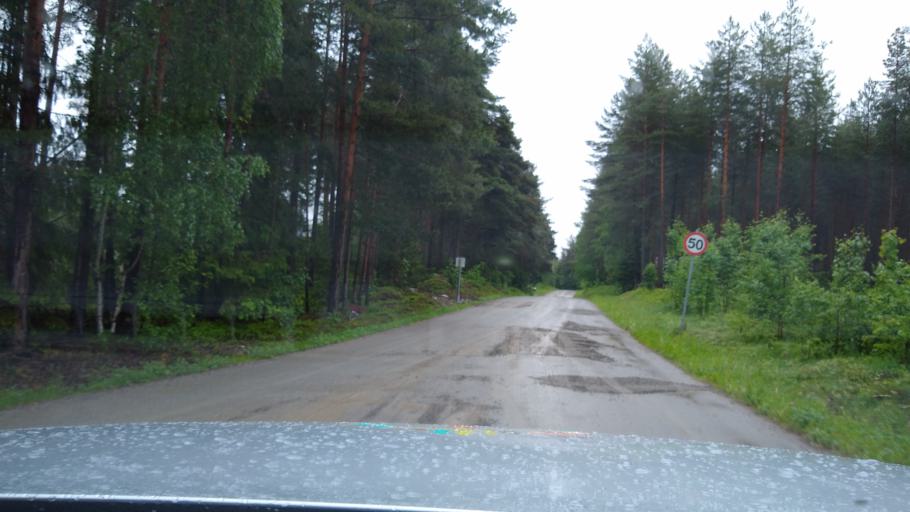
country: NO
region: Oppland
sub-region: Ringebu
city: Ringebu
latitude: 61.5442
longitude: 10.0998
